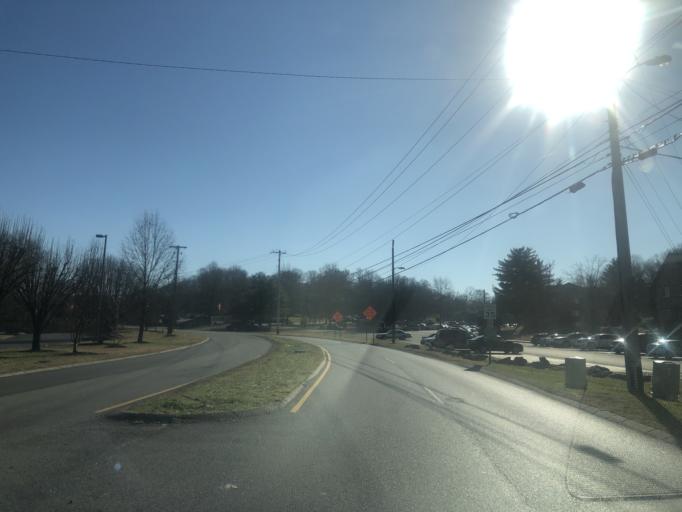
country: US
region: Tennessee
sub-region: Rutherford County
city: La Vergne
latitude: 36.0430
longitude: -86.6617
